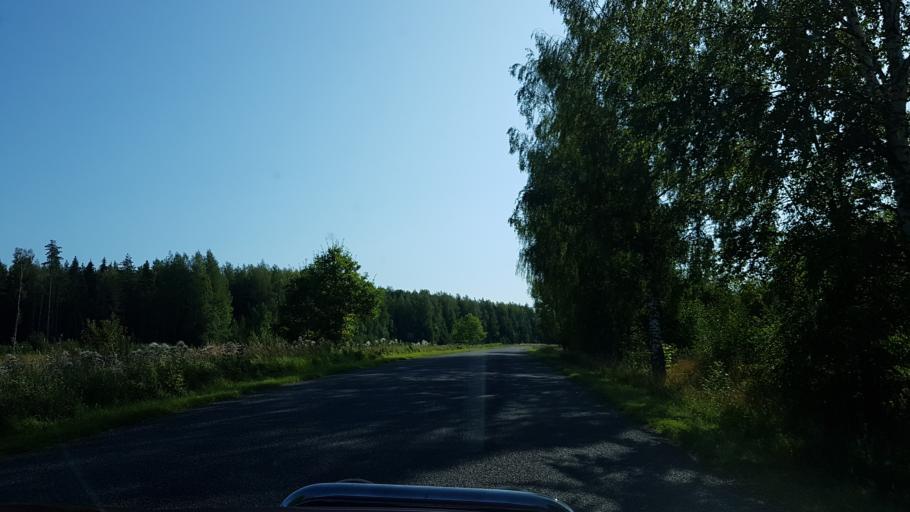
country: EE
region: Vorumaa
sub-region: Voru linn
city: Voru
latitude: 57.7305
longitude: 26.8343
